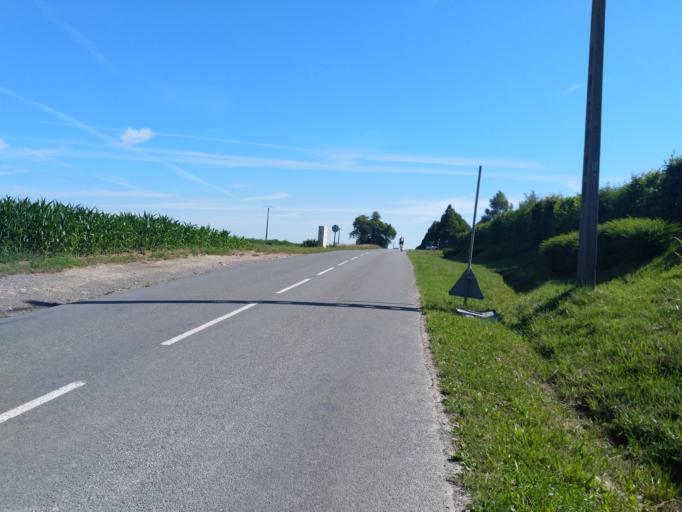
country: FR
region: Nord-Pas-de-Calais
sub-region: Departement du Nord
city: Bavay
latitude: 50.3137
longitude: 3.8114
